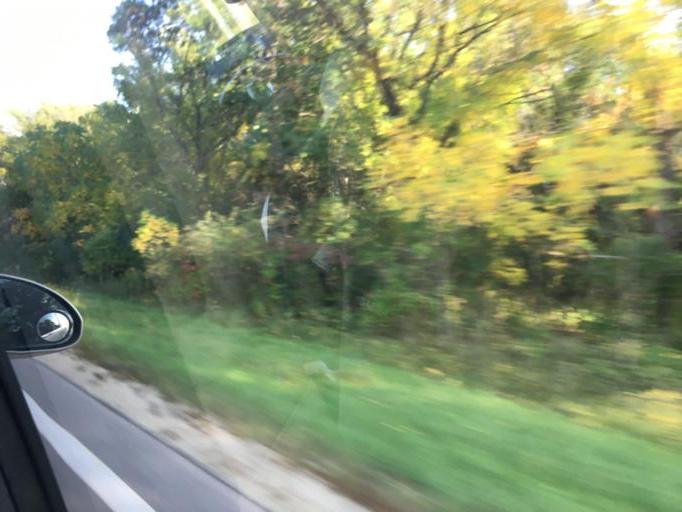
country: US
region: Minnesota
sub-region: Olmsted County
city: Rochester
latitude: 43.9926
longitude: -92.4178
